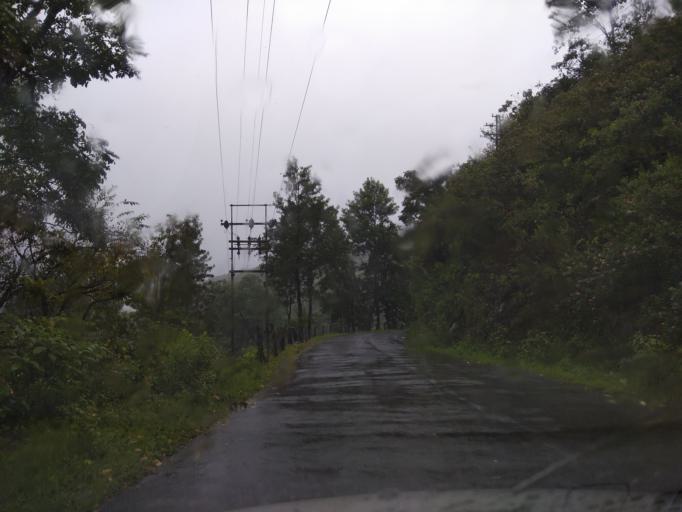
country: IN
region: Kerala
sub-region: Idukki
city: Munnar
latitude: 10.1272
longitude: 77.0559
